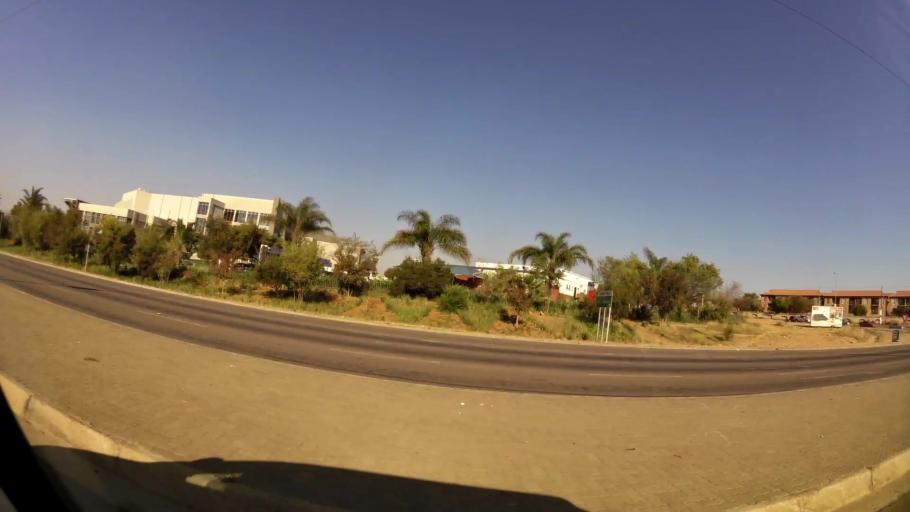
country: ZA
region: Gauteng
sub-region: City of Tshwane Metropolitan Municipality
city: Pretoria
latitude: -25.7777
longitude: 28.3449
